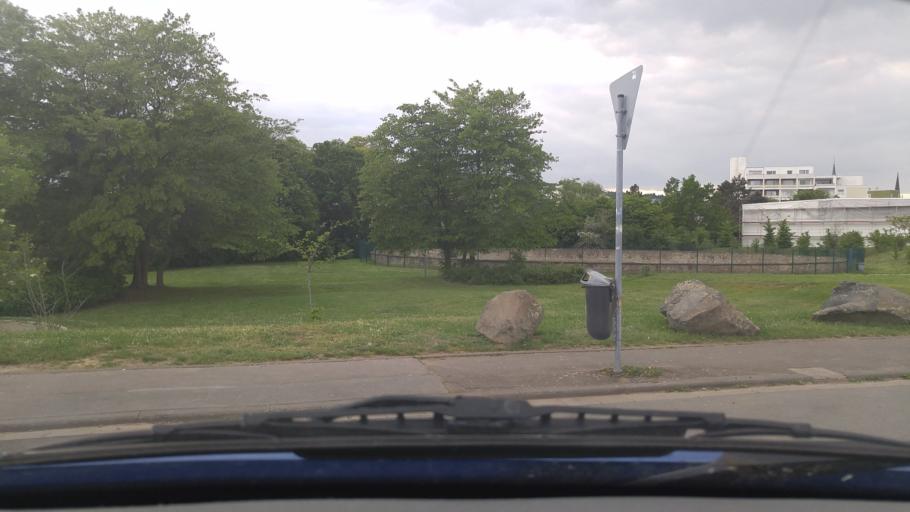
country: DE
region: Hesse
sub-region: Regierungsbezirk Darmstadt
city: Bad Nauheim
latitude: 50.3586
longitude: 8.7475
